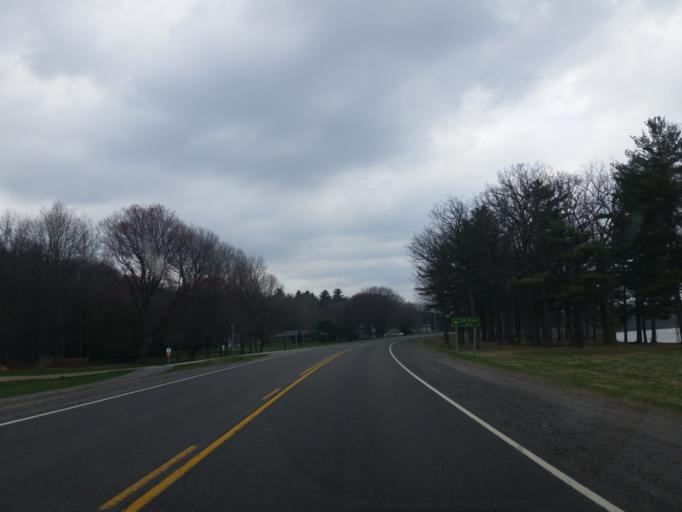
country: US
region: New York
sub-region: Jefferson County
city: Alexandria Bay
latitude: 44.4820
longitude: -75.8322
